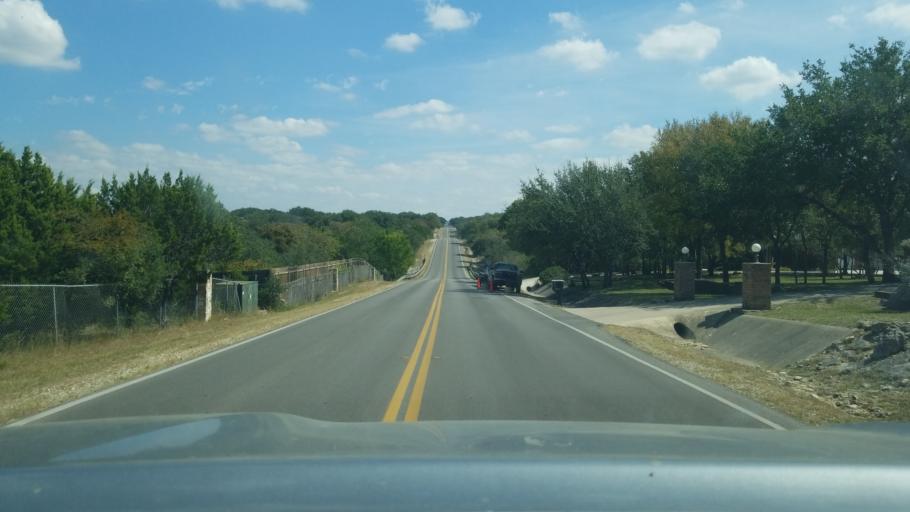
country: US
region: Texas
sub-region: Bexar County
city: Fair Oaks Ranch
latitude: 29.7311
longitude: -98.6516
